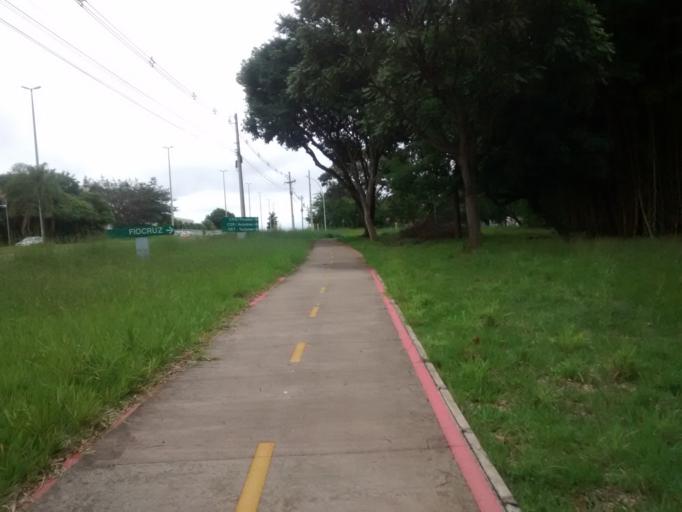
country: BR
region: Federal District
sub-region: Brasilia
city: Brasilia
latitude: -15.7735
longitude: -47.8718
